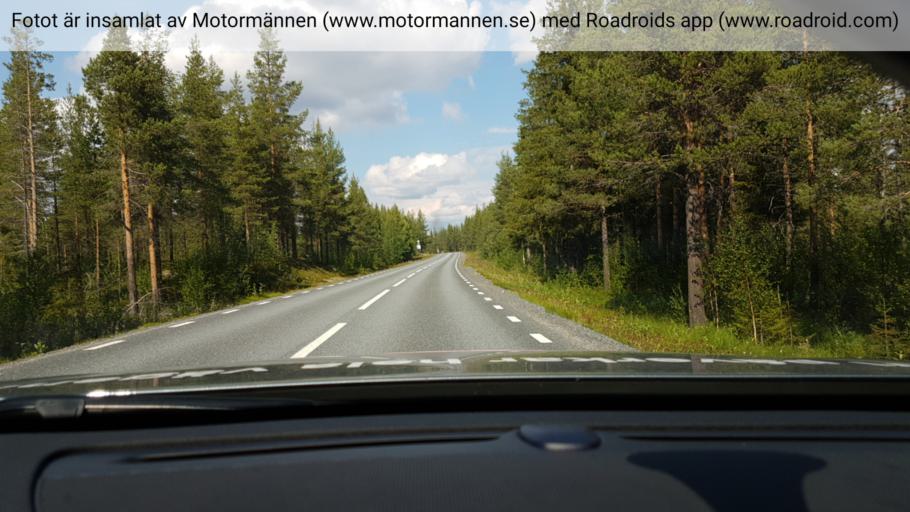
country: SE
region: Vaesterbotten
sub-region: Sorsele Kommun
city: Sorsele
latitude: 65.4920
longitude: 17.5539
